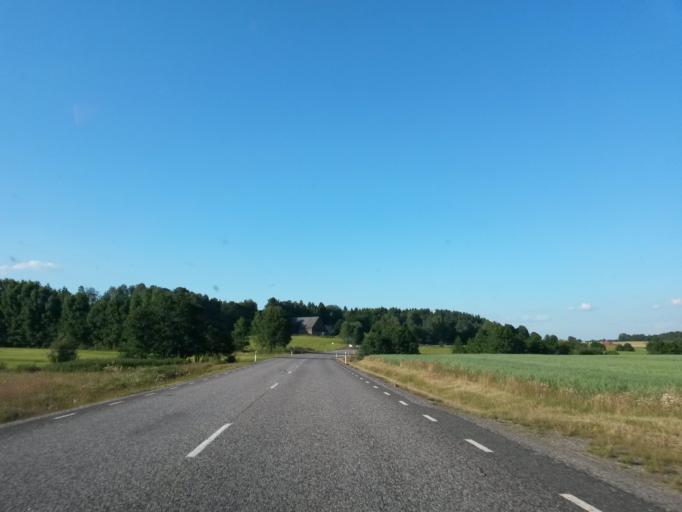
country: SE
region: Vaestra Goetaland
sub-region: Vargarda Kommun
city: Jonstorp
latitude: 58.0342
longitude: 12.6353
